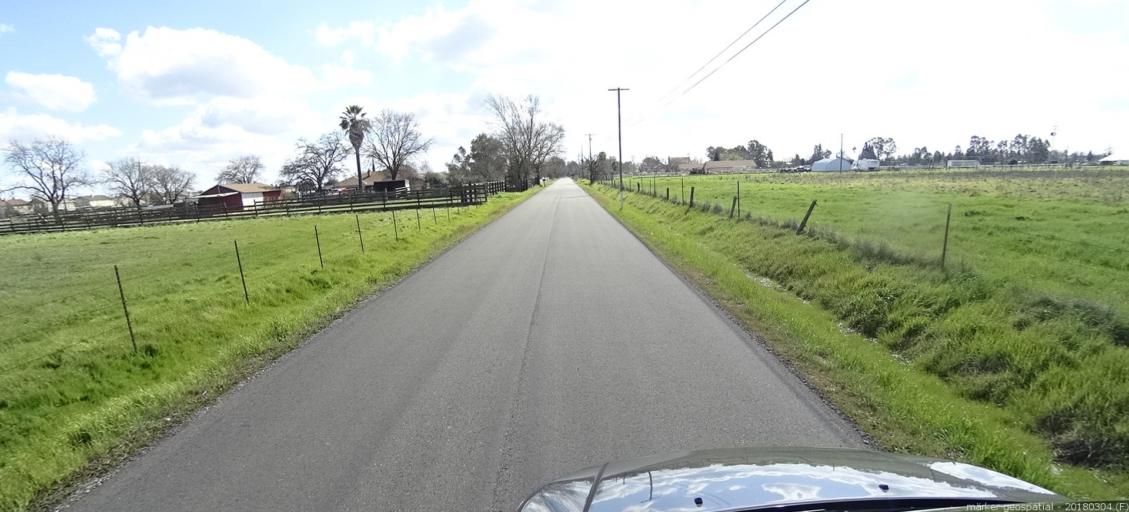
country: US
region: California
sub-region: Sacramento County
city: Vineyard
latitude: 38.4611
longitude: -121.3301
